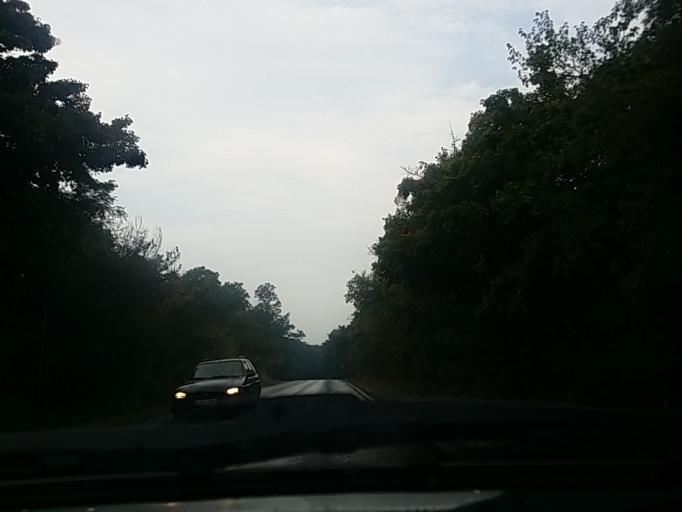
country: HU
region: Pest
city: Paty
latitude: 47.5016
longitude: 18.8647
